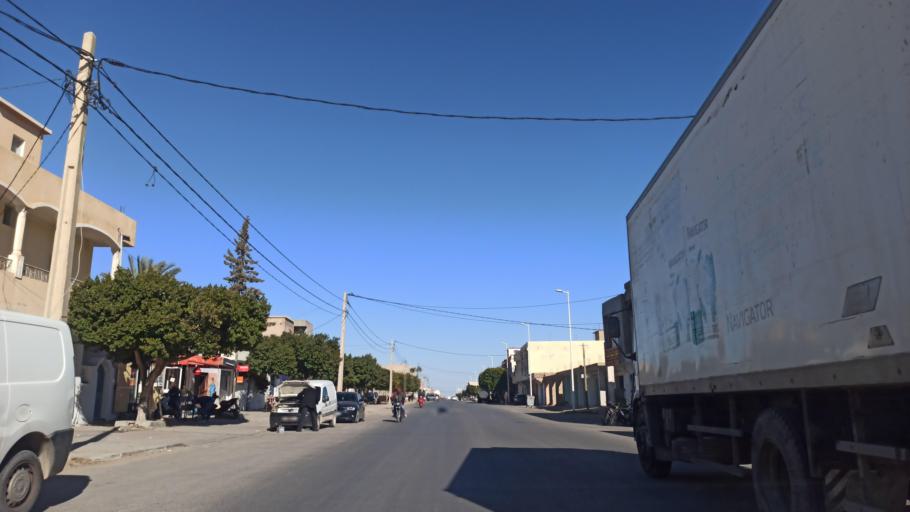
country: TN
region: Sidi Bu Zayd
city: Bi'r al Hufayy
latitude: 34.9353
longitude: 9.1986
